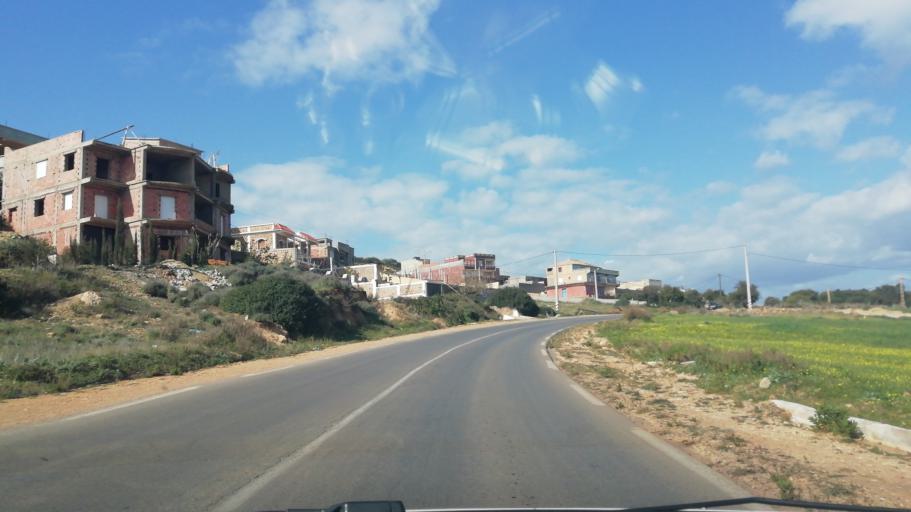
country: DZ
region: Relizane
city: Mazouna
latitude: 36.3258
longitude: 0.6959
